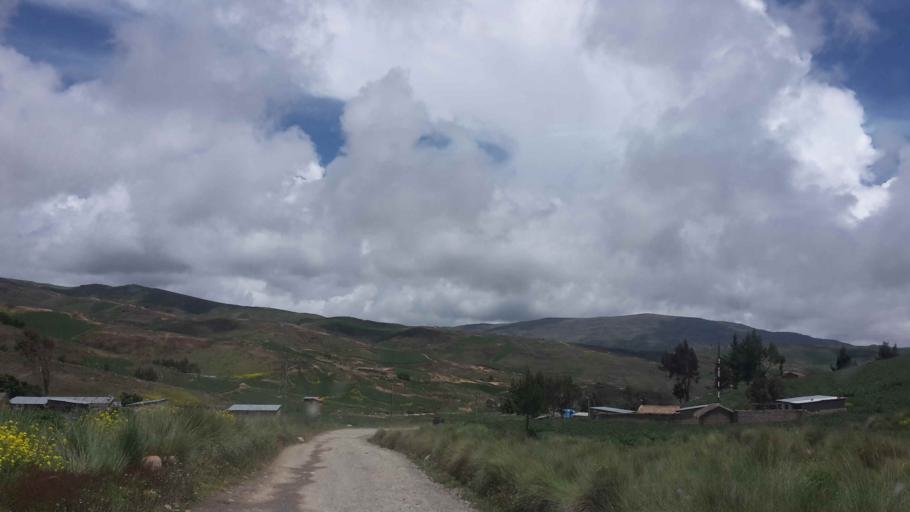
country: BO
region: Cochabamba
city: Cochabamba
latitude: -17.2165
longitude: -66.0834
